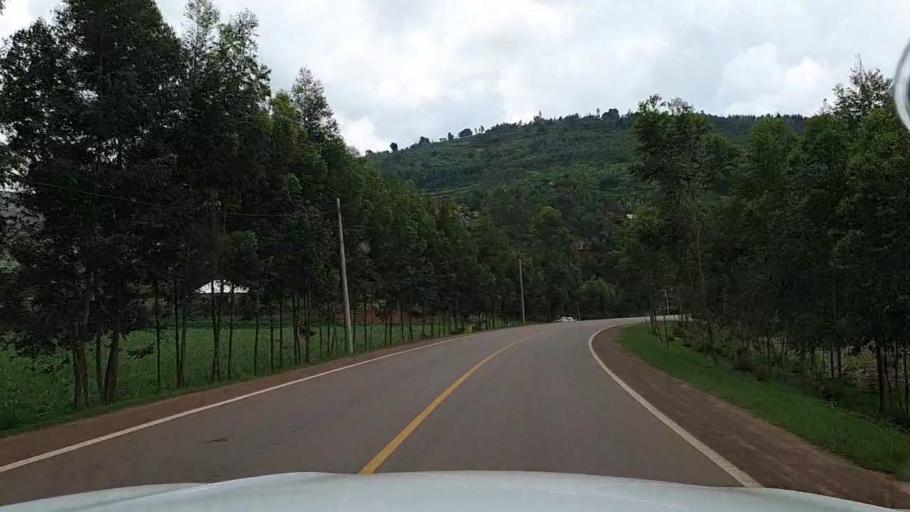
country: RW
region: Kigali
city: Kigali
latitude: -1.8123
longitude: 30.0974
